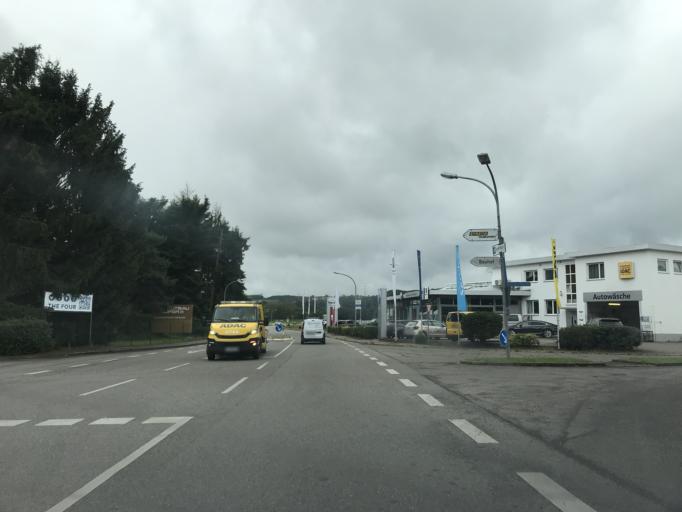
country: DE
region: Baden-Wuerttemberg
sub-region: Freiburg Region
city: Steinen
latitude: 47.6427
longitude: 7.7321
